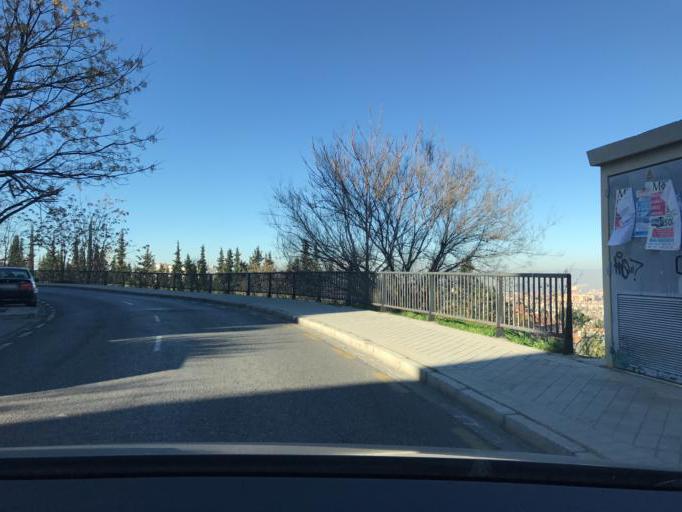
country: ES
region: Andalusia
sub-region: Provincia de Granada
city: Huetor Vega
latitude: 37.1592
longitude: -3.5779
